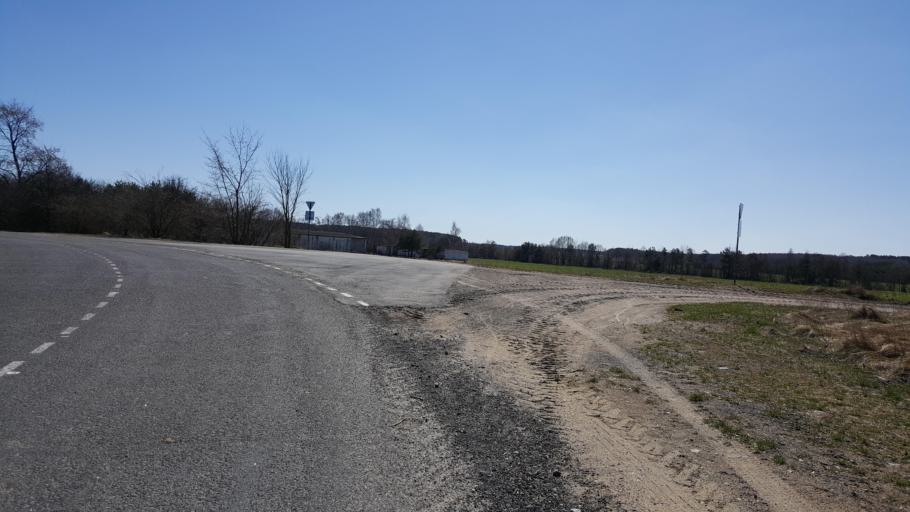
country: BY
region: Brest
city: Charnawchytsy
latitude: 52.2606
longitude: 23.8527
